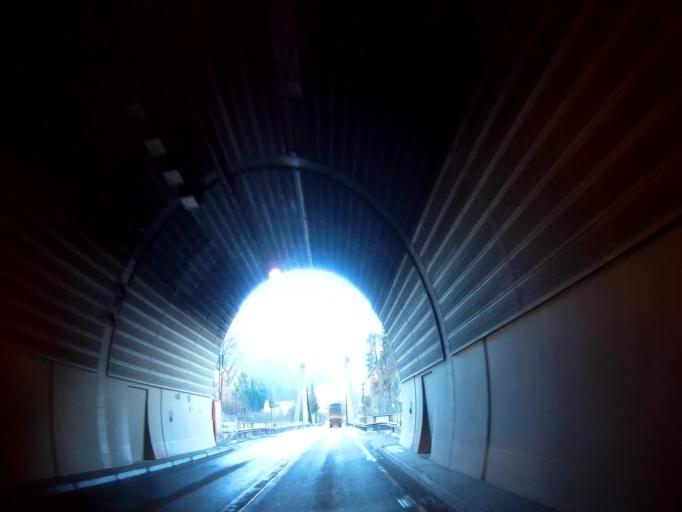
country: AT
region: Salzburg
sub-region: Politischer Bezirk Zell am See
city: Unken
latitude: 47.6521
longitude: 12.7388
